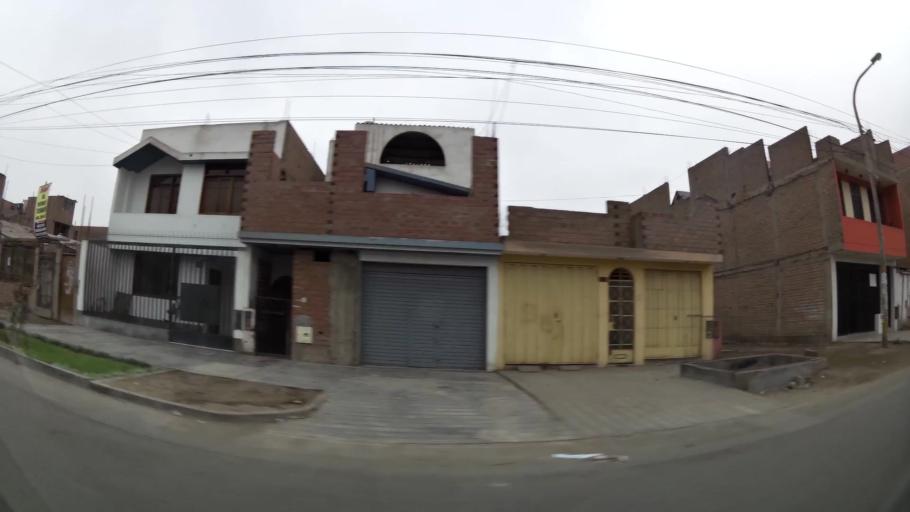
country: PE
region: Lima
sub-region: Lima
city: Urb. Santo Domingo
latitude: -11.9176
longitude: -77.0521
